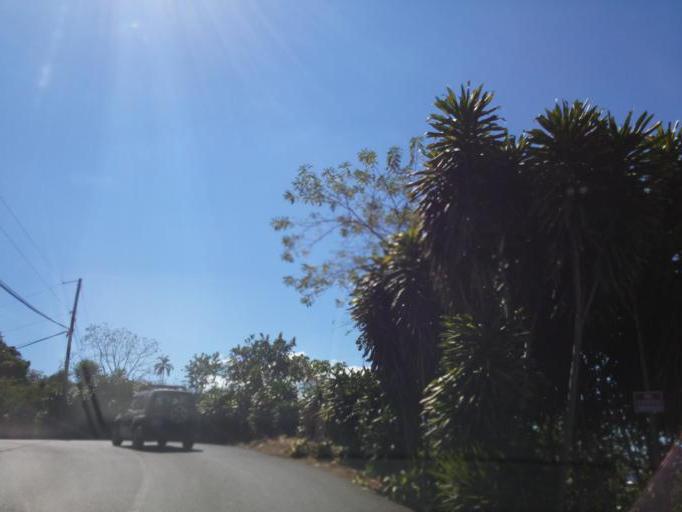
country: CR
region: San Jose
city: Palmichal
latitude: 9.8367
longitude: -84.2069
